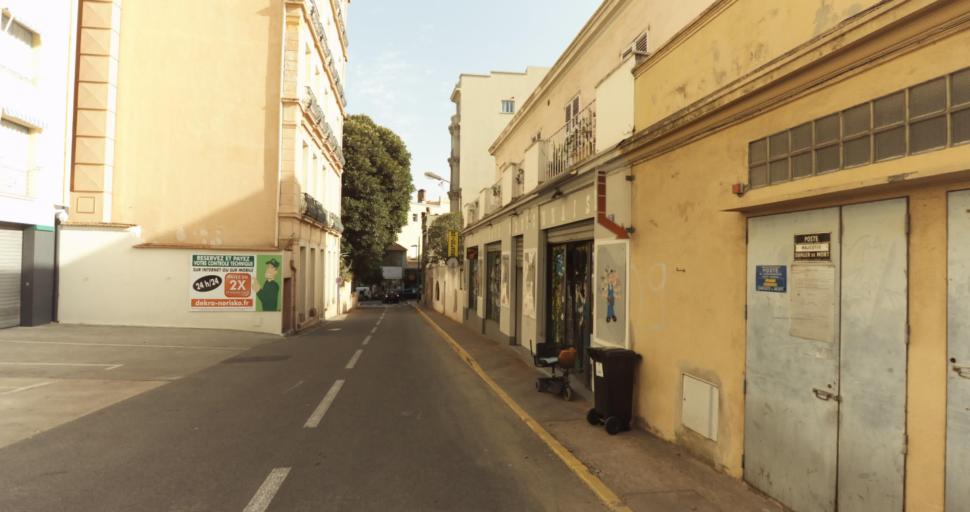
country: FR
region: Provence-Alpes-Cote d'Azur
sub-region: Departement des Alpes-Maritimes
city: Menton
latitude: 43.7754
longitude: 7.4973
